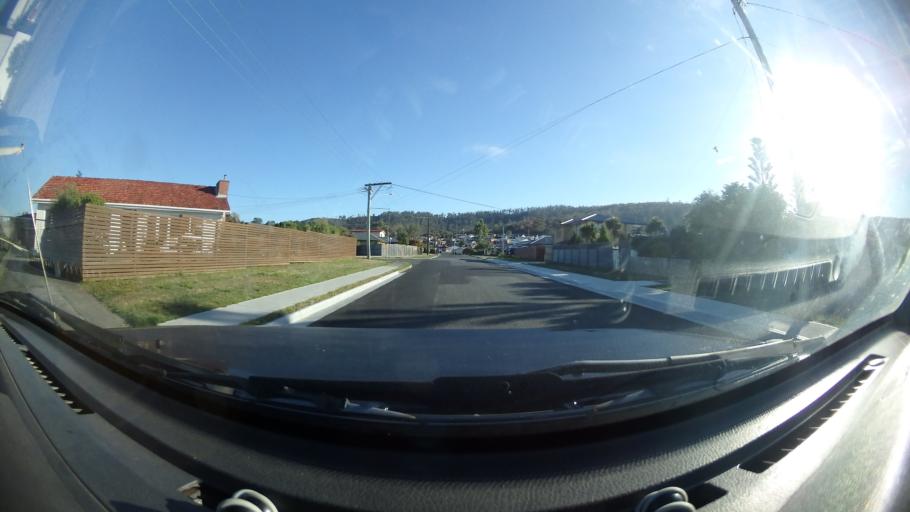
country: AU
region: Tasmania
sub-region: Clarence
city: Howrah
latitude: -42.8766
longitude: 147.3985
